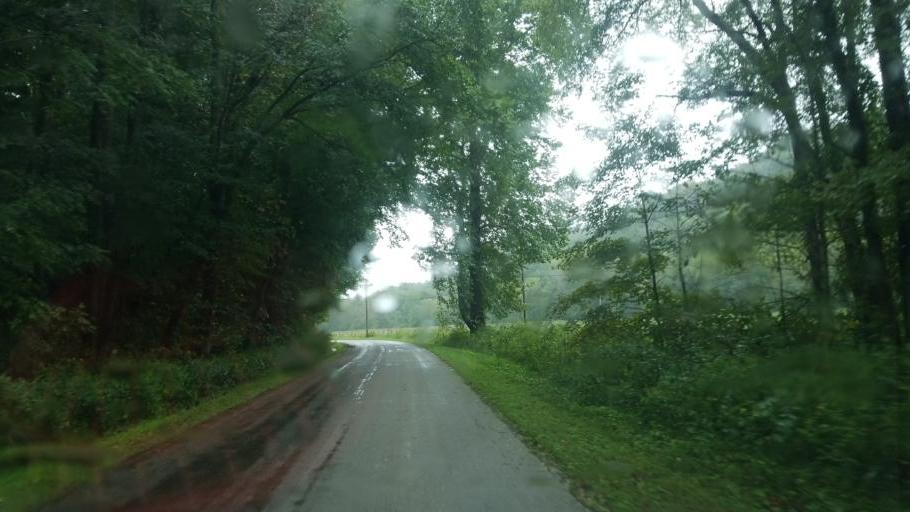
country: US
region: Ohio
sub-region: Adams County
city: Peebles
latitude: 38.8300
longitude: -83.2355
